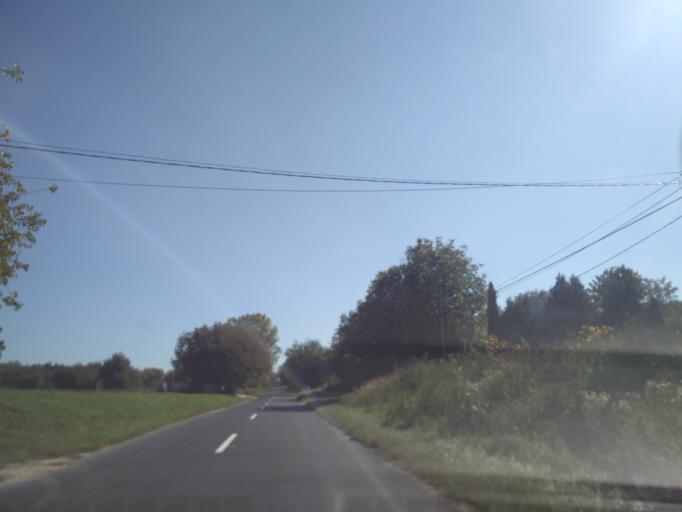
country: HU
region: Fejer
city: Lovasbereny
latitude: 47.2945
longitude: 18.5697
